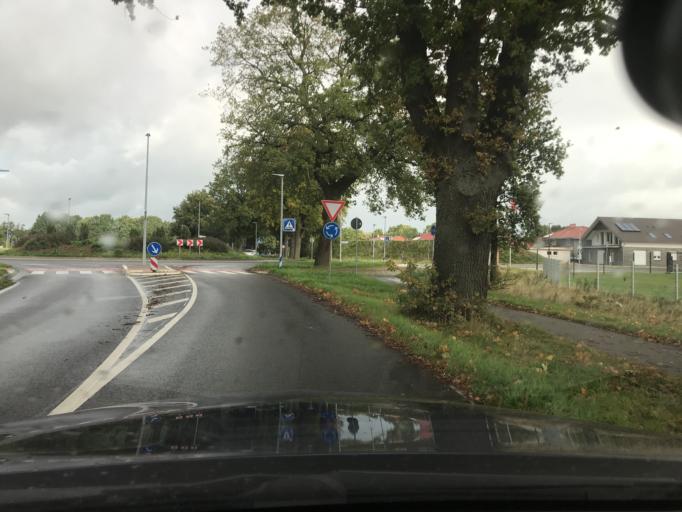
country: DE
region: Lower Saxony
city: Stade
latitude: 53.5708
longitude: 9.4721
